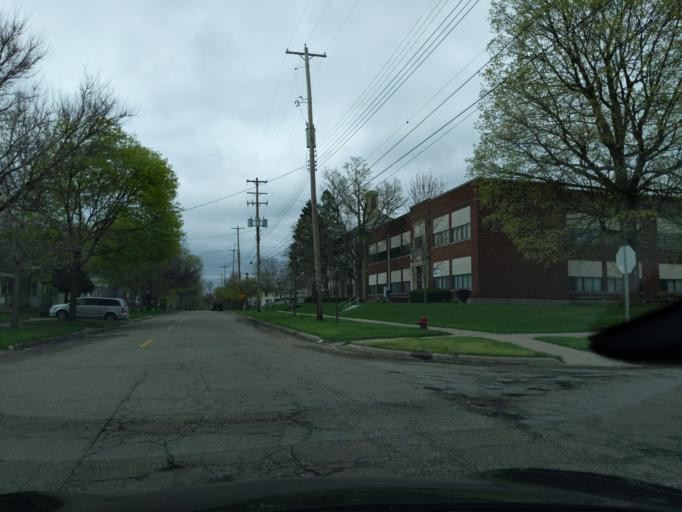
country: US
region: Michigan
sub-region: Ingham County
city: Lansing
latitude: 42.7447
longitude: -84.5569
